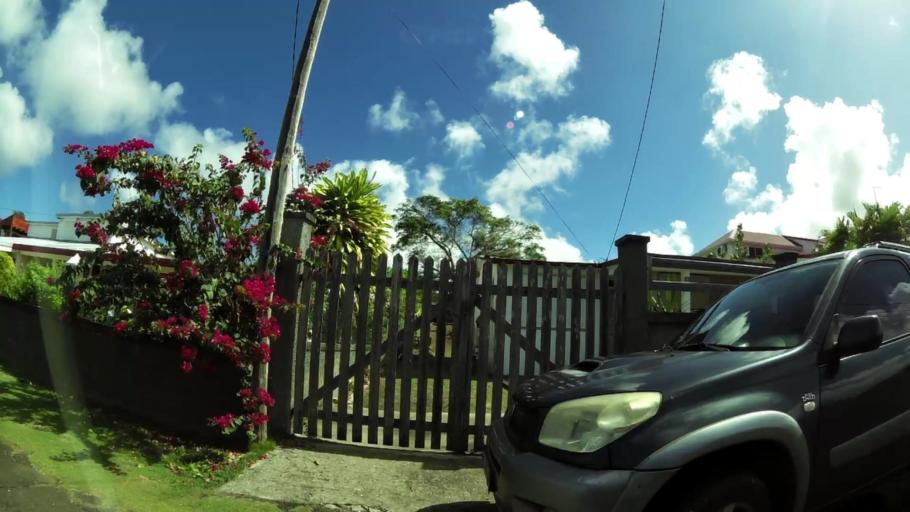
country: GP
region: Guadeloupe
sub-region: Guadeloupe
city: Anse-Bertrand
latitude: 16.4685
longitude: -61.5142
